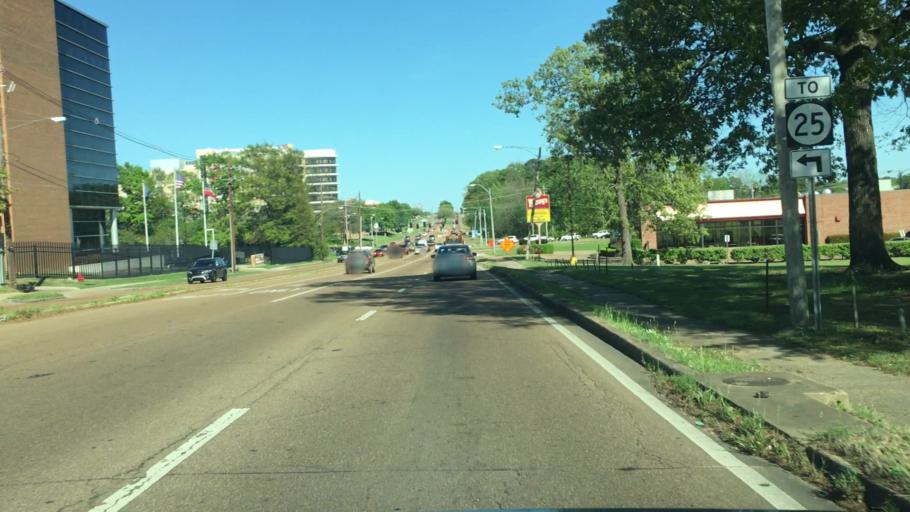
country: US
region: Mississippi
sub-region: Hinds County
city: Jackson
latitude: 32.3267
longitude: -90.1780
